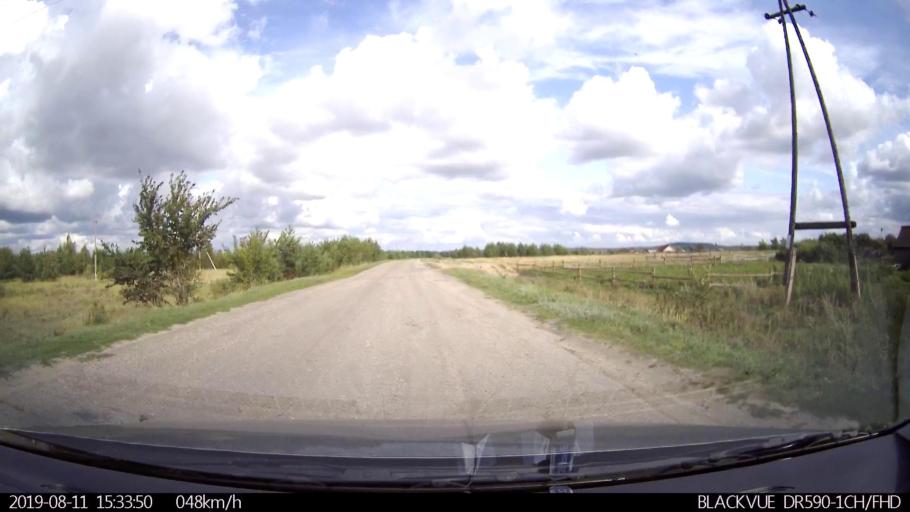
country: RU
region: Ulyanovsk
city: Ignatovka
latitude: 53.8622
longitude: 47.5880
